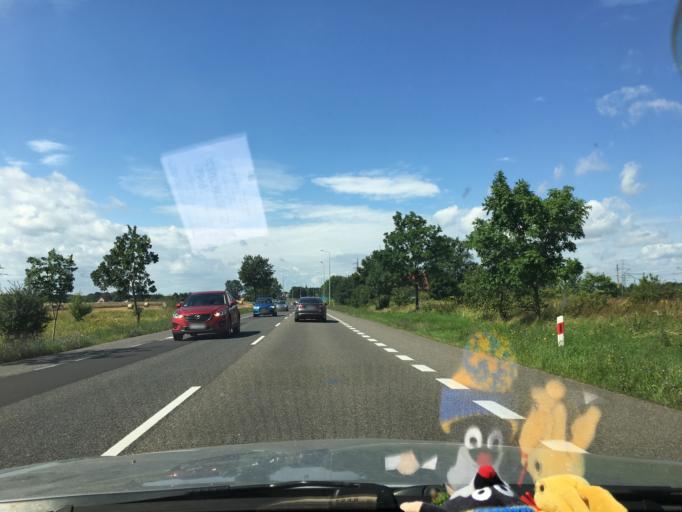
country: PL
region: West Pomeranian Voivodeship
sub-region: Powiat kamienski
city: Wolin
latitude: 53.8447
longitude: 14.6397
